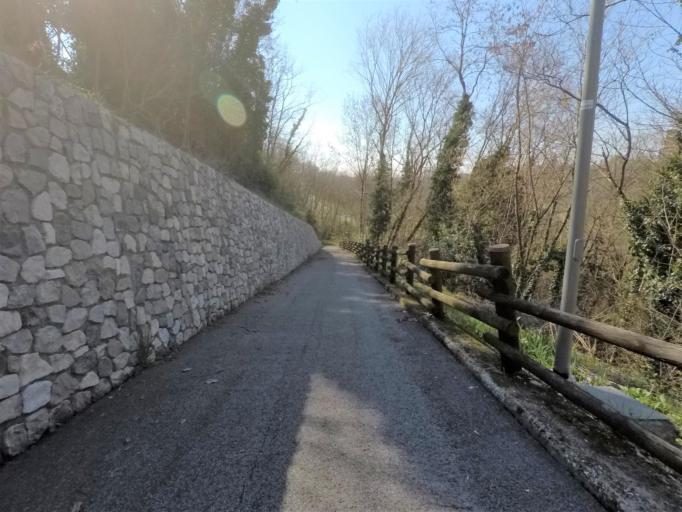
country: IT
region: Friuli Venezia Giulia
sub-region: Provincia di Udine
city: Orsaria
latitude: 46.0381
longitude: 13.3866
